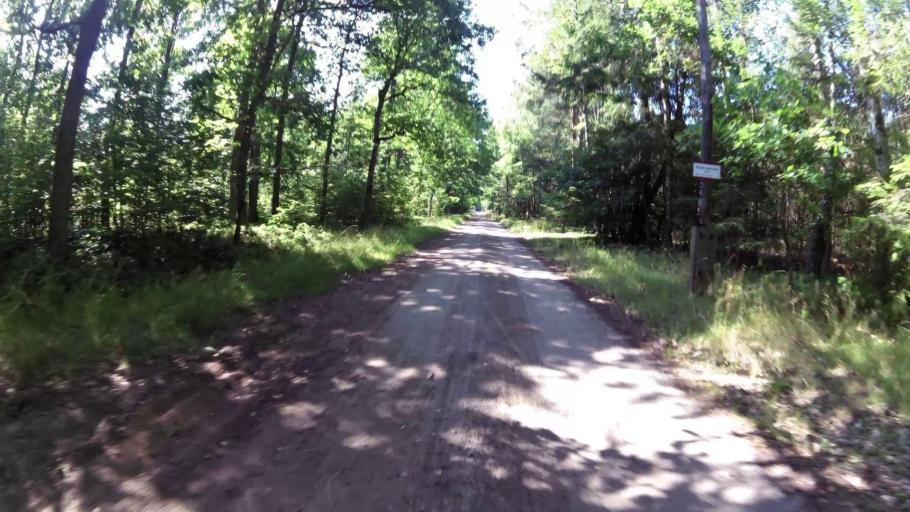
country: PL
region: West Pomeranian Voivodeship
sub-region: Powiat drawski
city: Czaplinek
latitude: 53.4137
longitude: 16.2569
